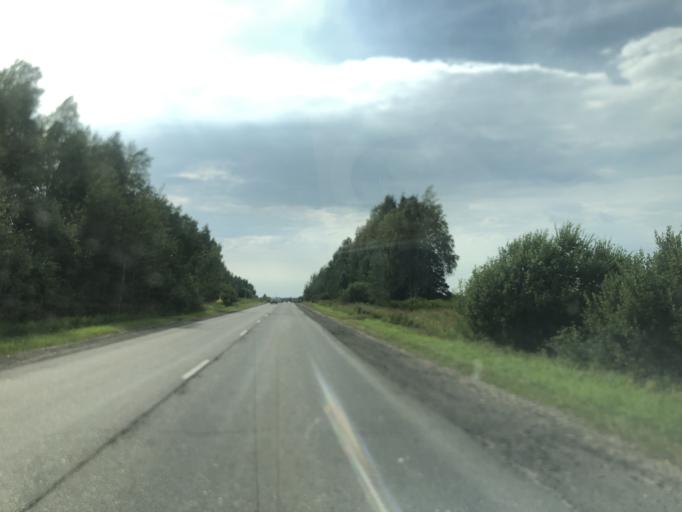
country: RU
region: Ivanovo
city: Shuya
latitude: 56.8562
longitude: 41.5197
